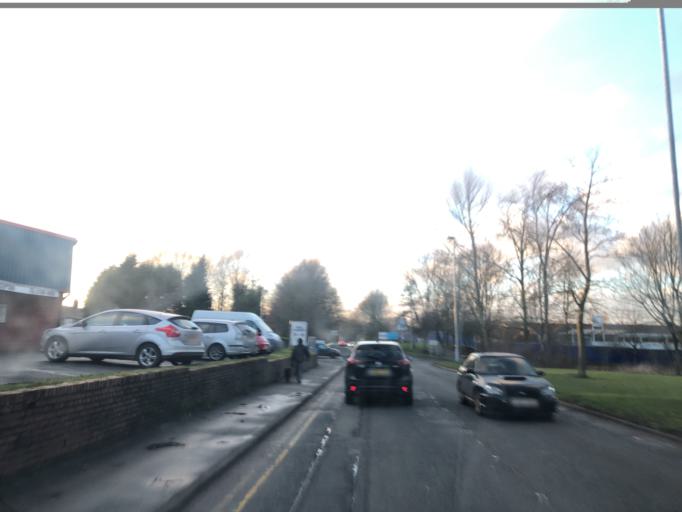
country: GB
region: England
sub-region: Cheshire West and Chester
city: Marston
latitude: 53.2641
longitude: -2.5039
